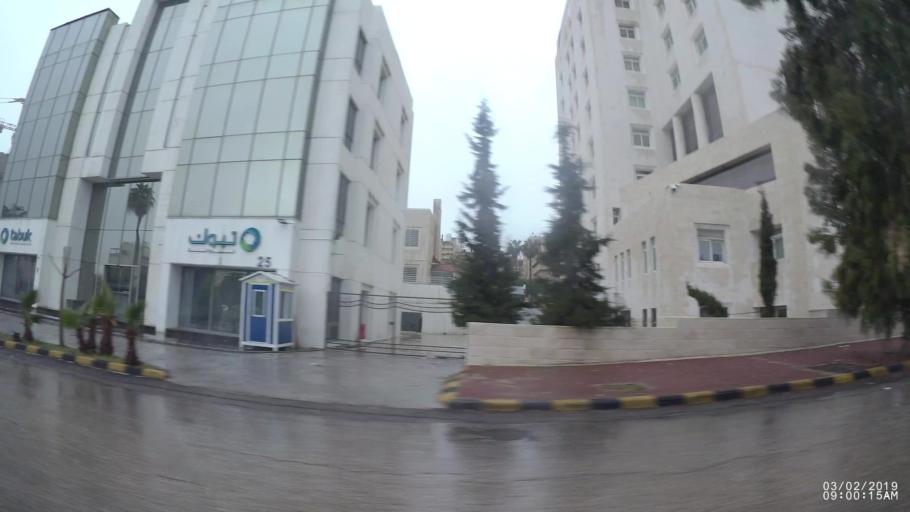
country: JO
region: Amman
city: Al Jubayhah
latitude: 31.9672
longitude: 35.8808
